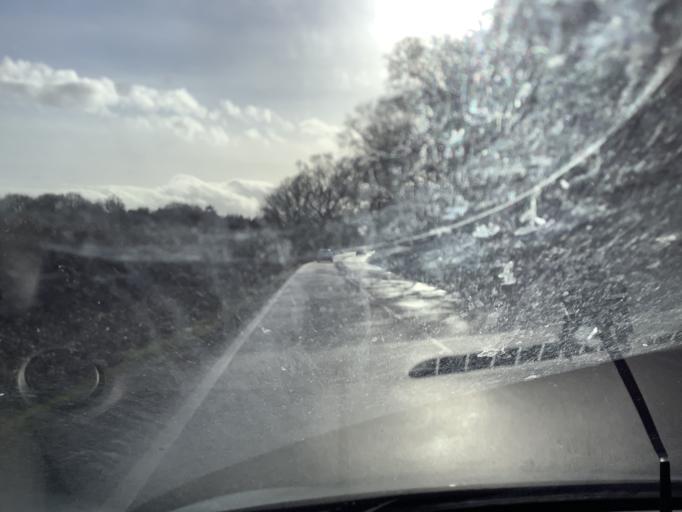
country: GB
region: England
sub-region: Hampshire
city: Hythe
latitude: 50.8253
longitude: -1.4348
